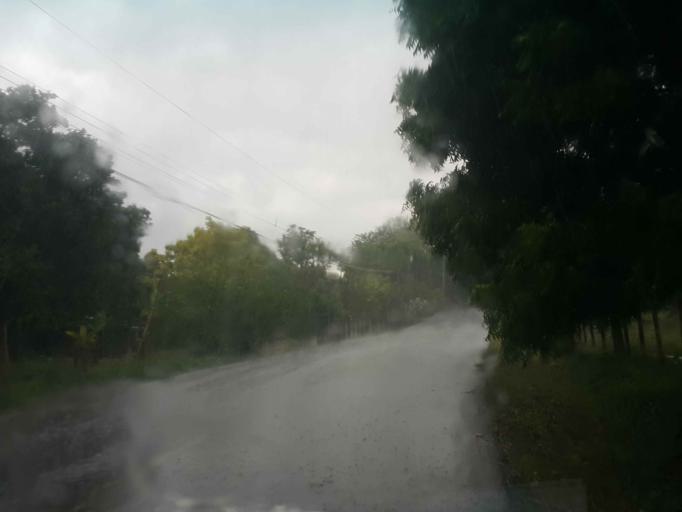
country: CR
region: Puntarenas
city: Miramar
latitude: 10.1258
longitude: -84.8302
